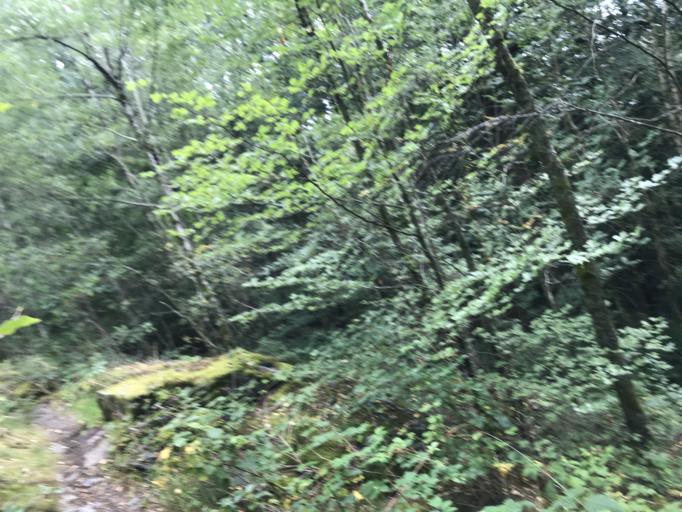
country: FR
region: Champagne-Ardenne
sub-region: Departement des Ardennes
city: Montherme
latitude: 49.8926
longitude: 4.7592
